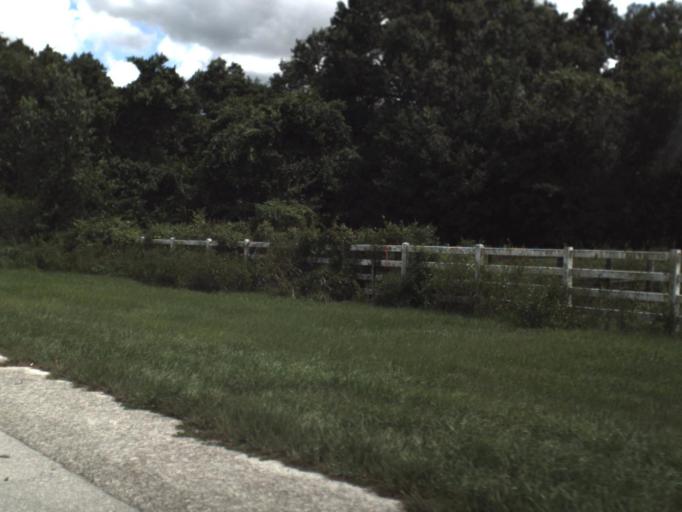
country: US
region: Florida
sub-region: Polk County
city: Fort Meade
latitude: 27.7335
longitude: -81.6892
